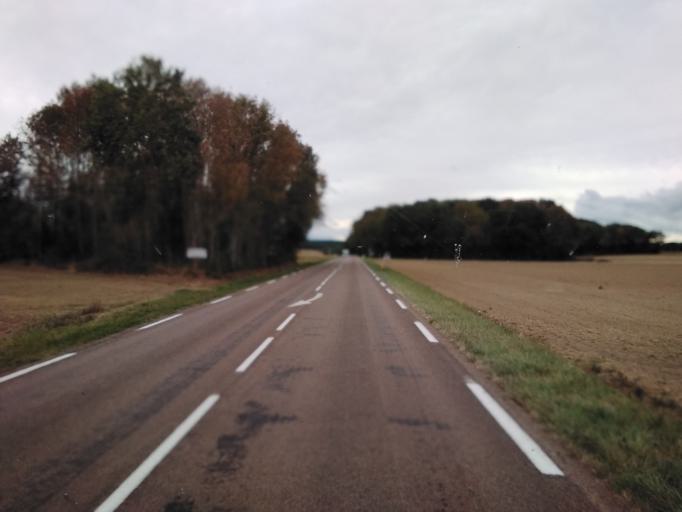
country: FR
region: Champagne-Ardenne
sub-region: Departement de l'Aube
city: Vendeuvre-sur-Barse
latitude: 48.2034
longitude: 4.4422
